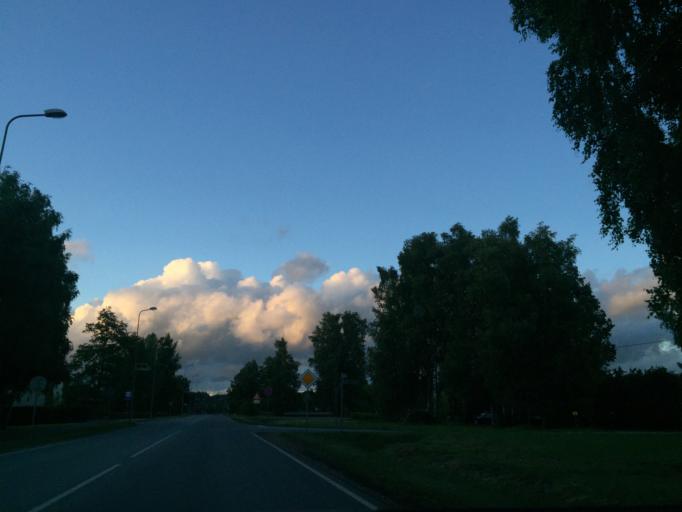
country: LV
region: Saulkrastu
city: Saulkrasti
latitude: 57.3147
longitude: 24.4163
